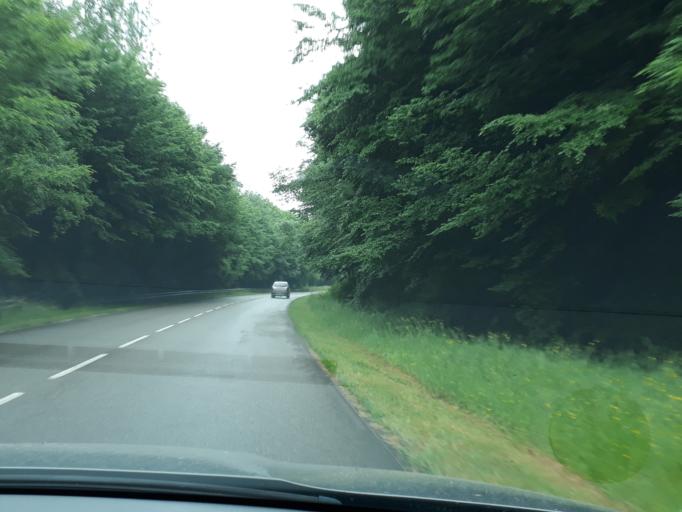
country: FR
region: Limousin
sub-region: Departement de la Correze
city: Cosnac
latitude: 45.1537
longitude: 1.6283
